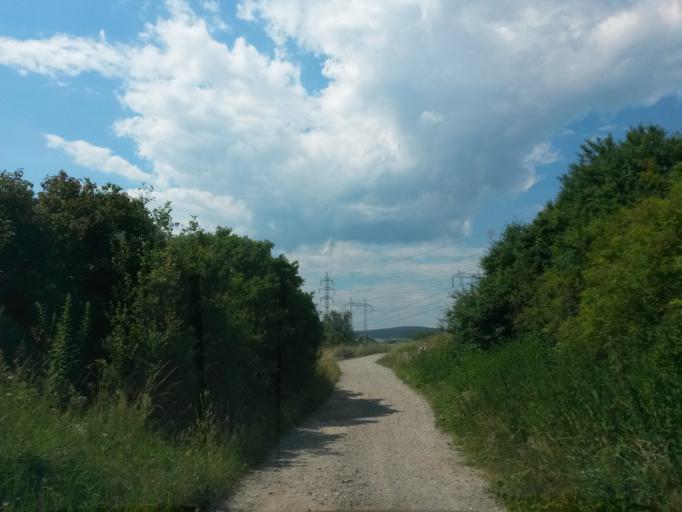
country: SK
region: Kosicky
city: Spisska Nova Ves
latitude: 48.9502
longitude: 20.5949
